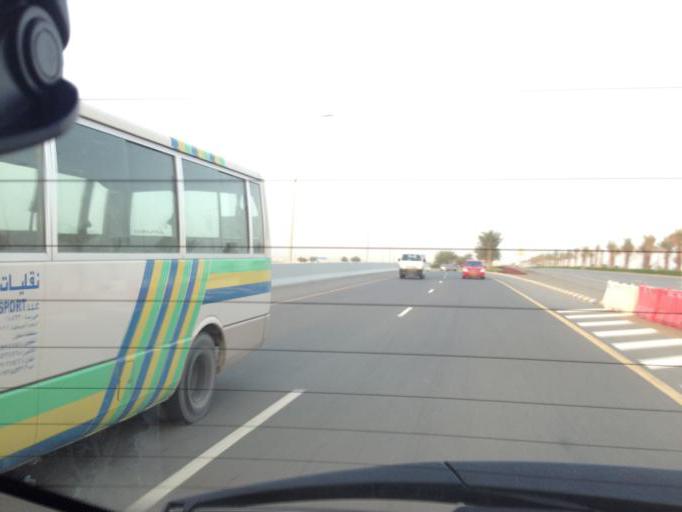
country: OM
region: Muhafazat Masqat
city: Bawshar
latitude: 23.6030
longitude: 58.3168
